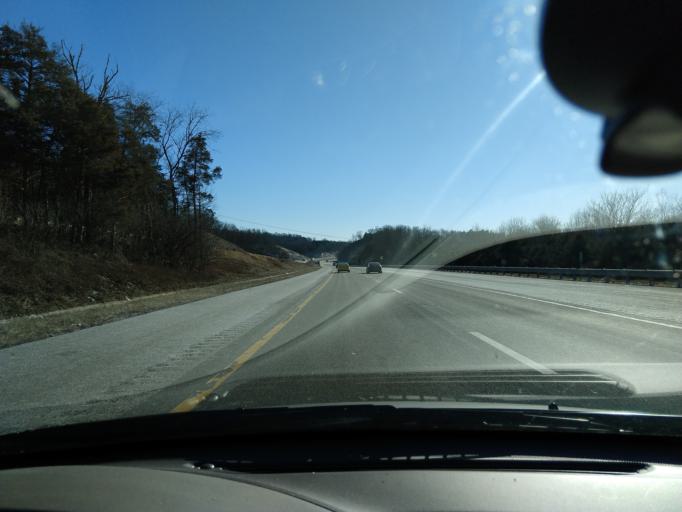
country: US
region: Virginia
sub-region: Rockbridge County
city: East Lexington
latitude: 37.7844
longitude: -79.4007
